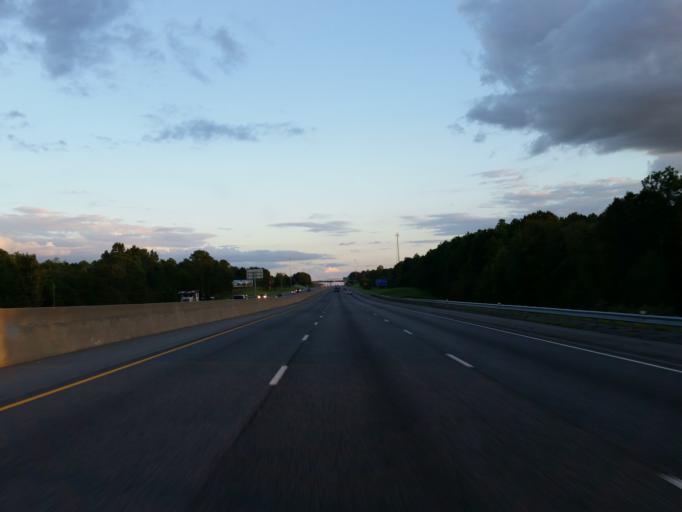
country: US
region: Georgia
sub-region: Tift County
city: Tifton
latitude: 31.5579
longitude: -83.5386
